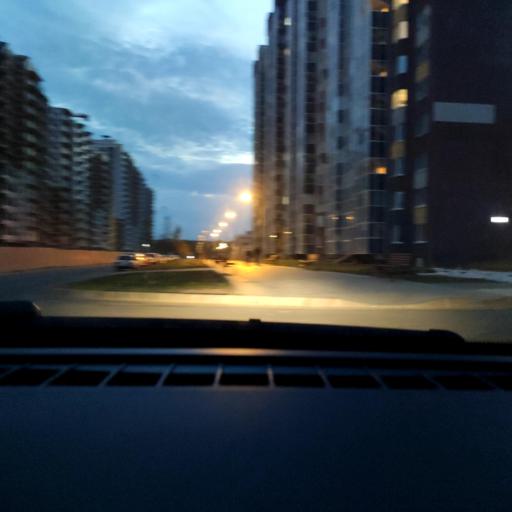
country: RU
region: Voronezj
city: Voronezh
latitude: 51.7140
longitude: 39.2698
